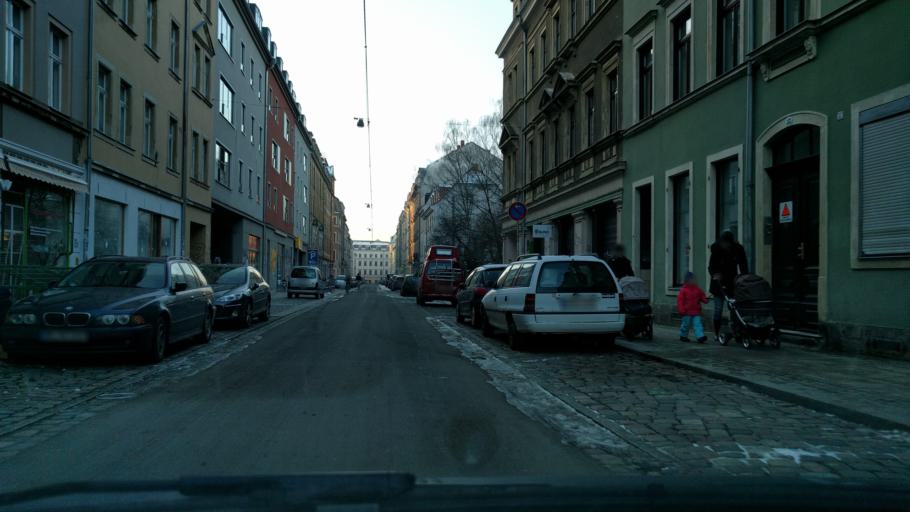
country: DE
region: Saxony
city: Albertstadt
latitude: 51.0678
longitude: 13.7584
